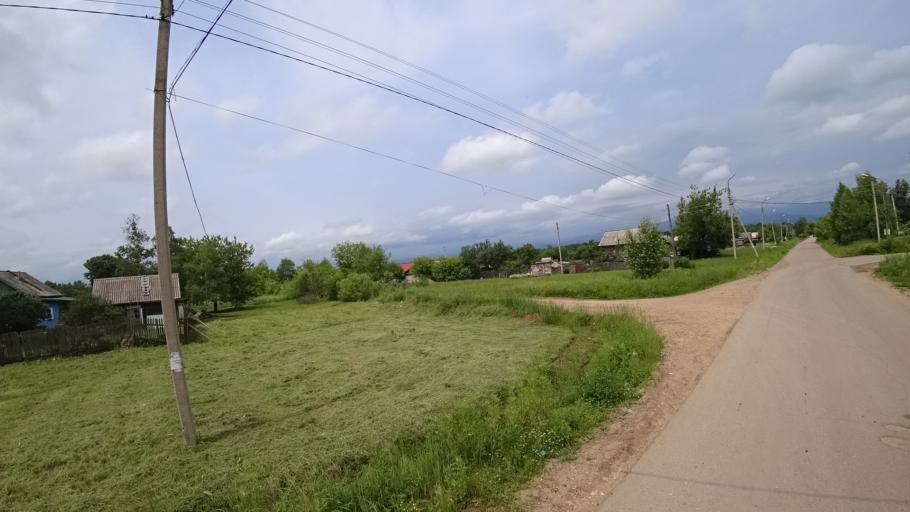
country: RU
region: Primorskiy
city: Novosysoyevka
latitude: 44.2351
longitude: 133.3591
